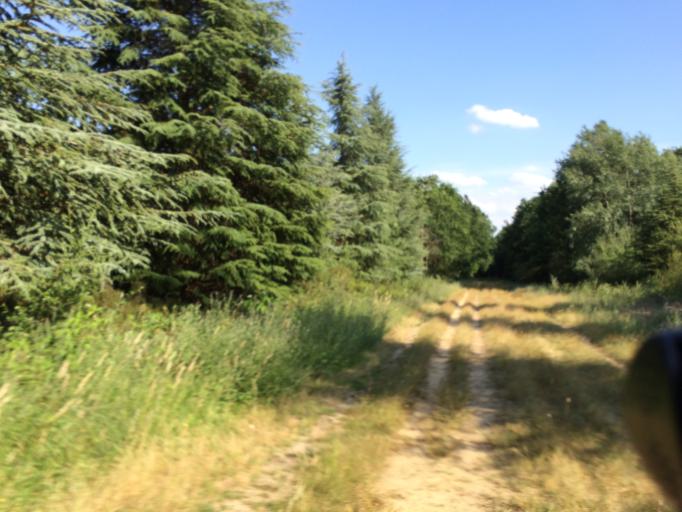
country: FR
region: Ile-de-France
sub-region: Departement de l'Essonne
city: Soisy-sur-Seine
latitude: 48.6741
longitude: 2.4533
